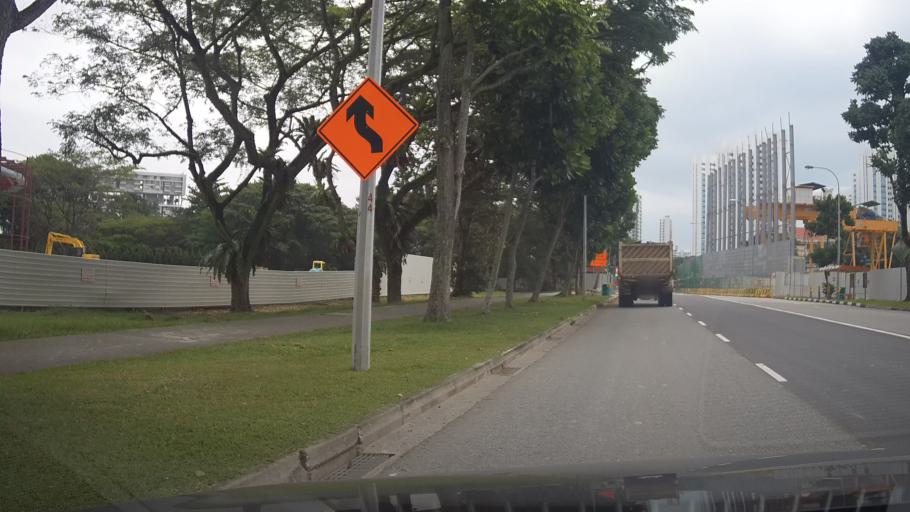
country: SG
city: Singapore
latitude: 1.2980
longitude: 103.8784
